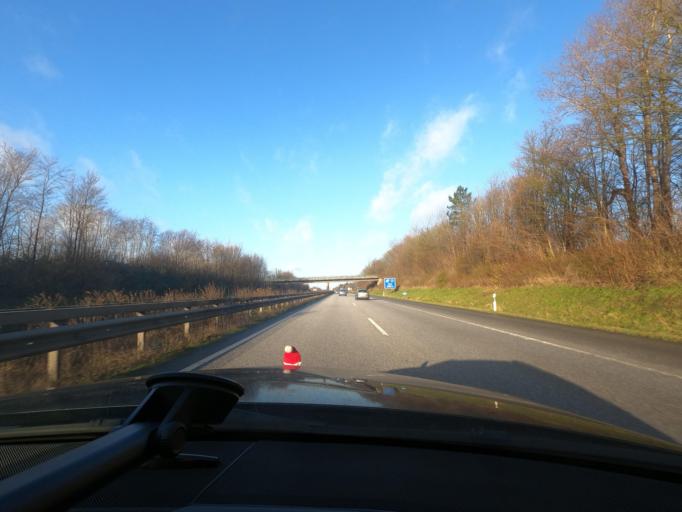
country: DE
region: Schleswig-Holstein
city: Tarp
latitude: 54.6530
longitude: 9.4350
